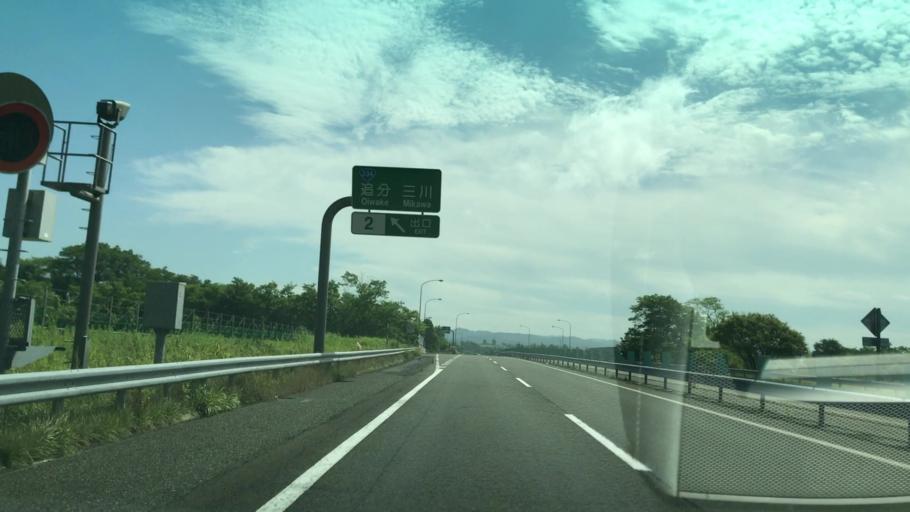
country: JP
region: Hokkaido
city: Chitose
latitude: 42.8931
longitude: 141.8107
